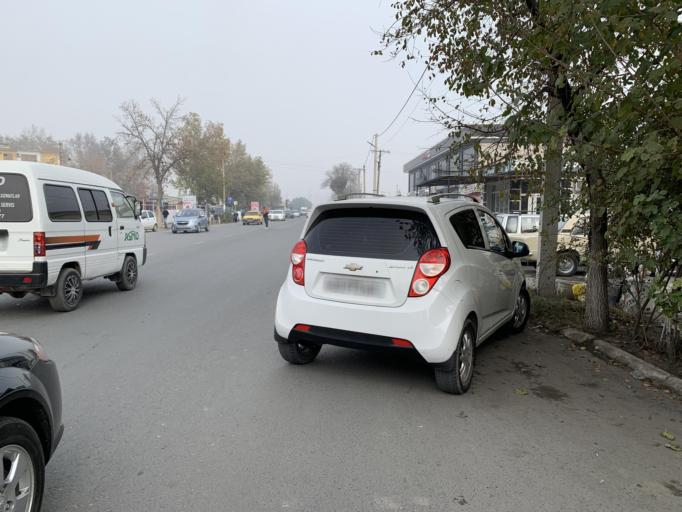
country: UZ
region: Fergana
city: Qo`qon
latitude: 40.5467
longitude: 70.9566
